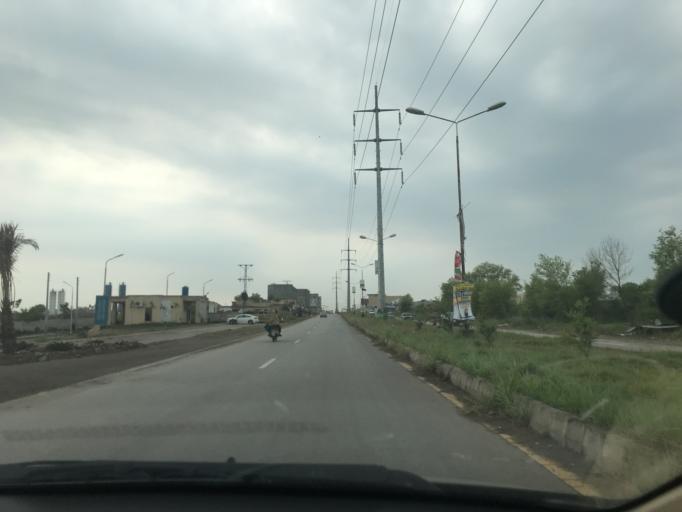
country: PK
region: Islamabad
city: Islamabad
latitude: 33.6876
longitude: 73.1673
